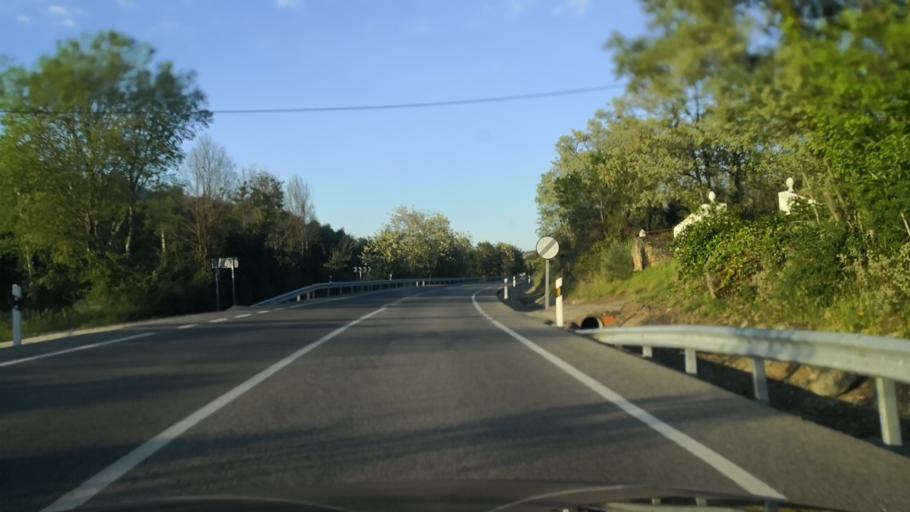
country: ES
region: Extremadura
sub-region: Provincia de Caceres
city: Valencia de Alcantara
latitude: 39.3669
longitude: -7.2699
